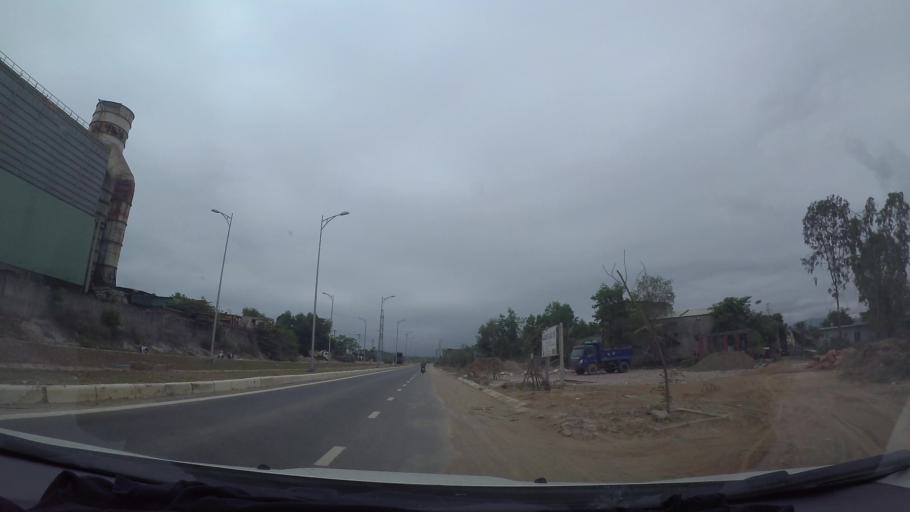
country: VN
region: Da Nang
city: Lien Chieu
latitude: 16.0868
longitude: 108.1042
